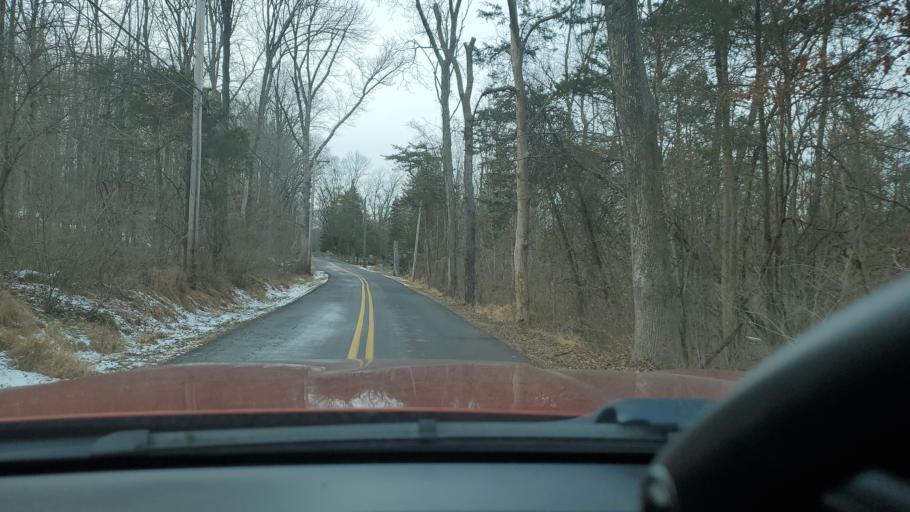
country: US
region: Pennsylvania
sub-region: Montgomery County
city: Woxall
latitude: 40.3220
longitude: -75.5023
